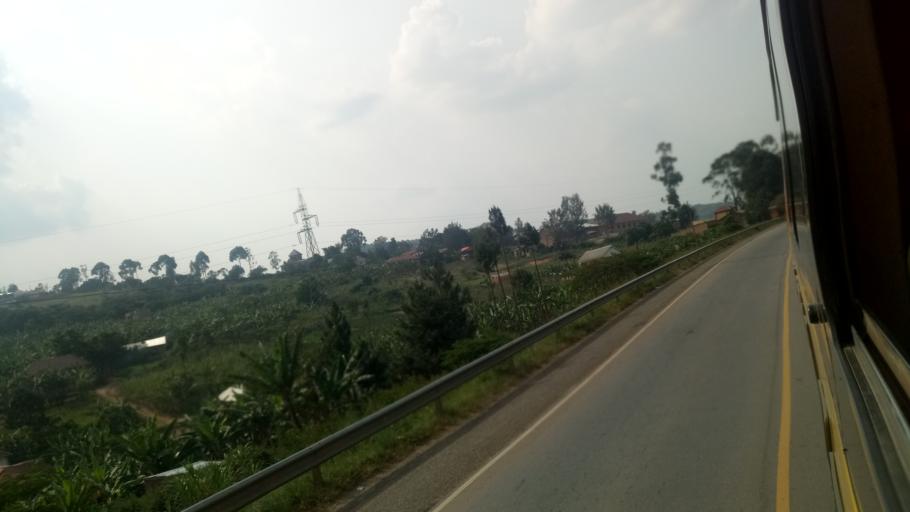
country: UG
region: Western Region
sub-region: Mbarara District
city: Mbarara
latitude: -0.5345
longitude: 30.7159
